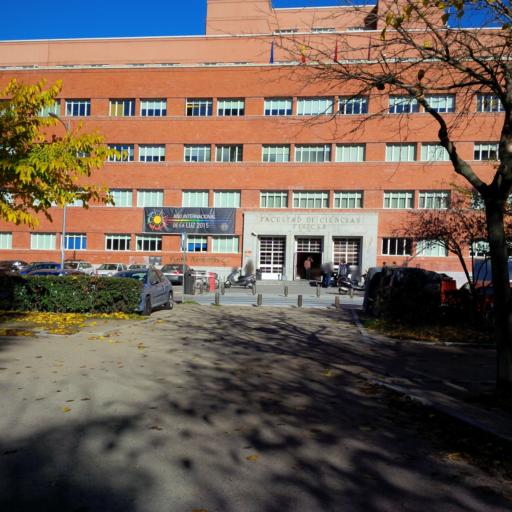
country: ES
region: Madrid
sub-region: Provincia de Madrid
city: Moncloa-Aravaca
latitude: 40.4505
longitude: -3.7260
